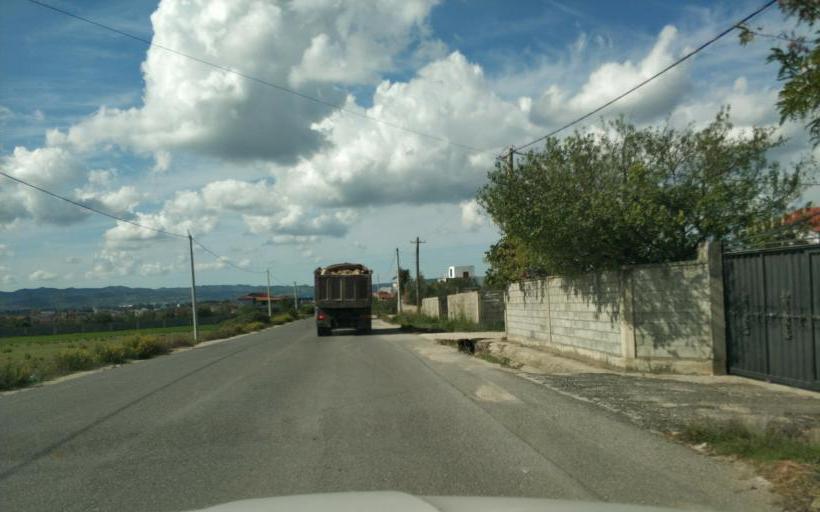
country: AL
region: Durres
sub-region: Rrethi i Krujes
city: Fushe-Kruje
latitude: 41.4780
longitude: 19.7379
